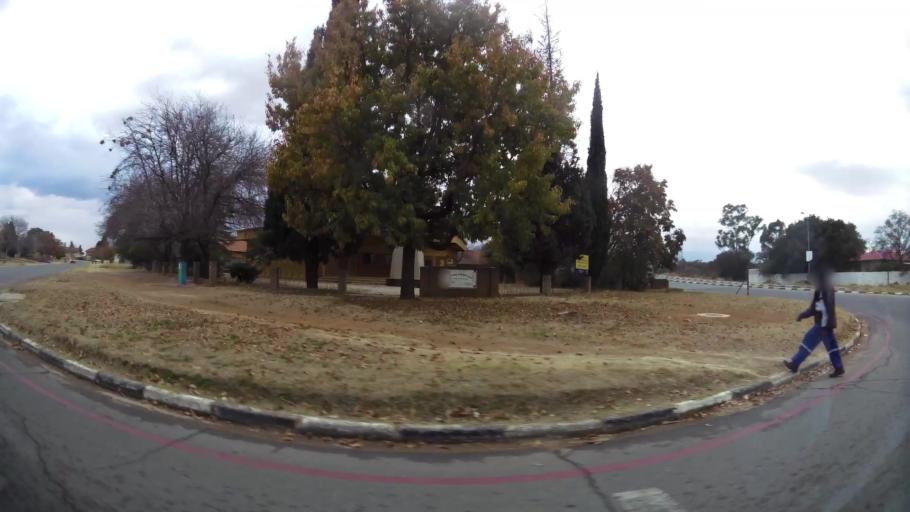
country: ZA
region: Orange Free State
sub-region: Lejweleputswa District Municipality
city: Welkom
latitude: -27.9607
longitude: 26.7253
